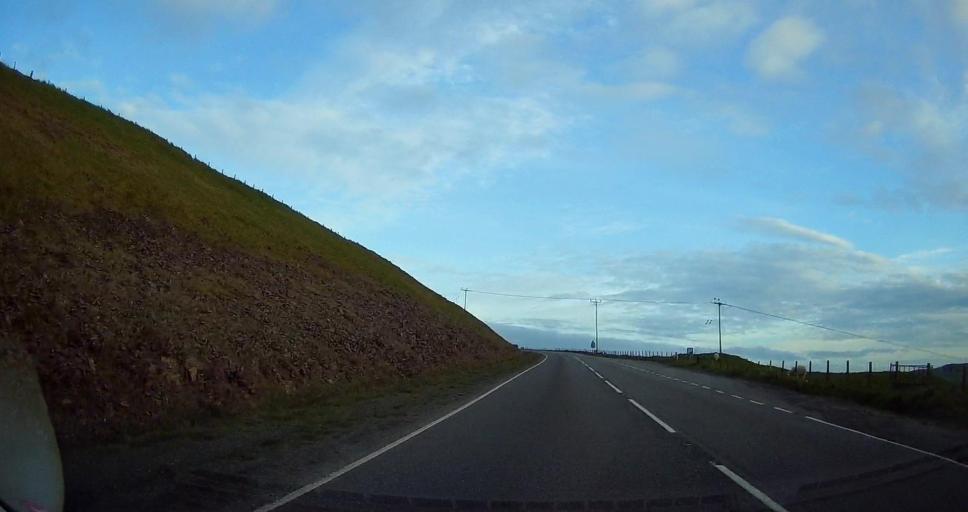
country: GB
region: Scotland
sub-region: Shetland Islands
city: Lerwick
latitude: 60.1831
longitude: -1.2244
